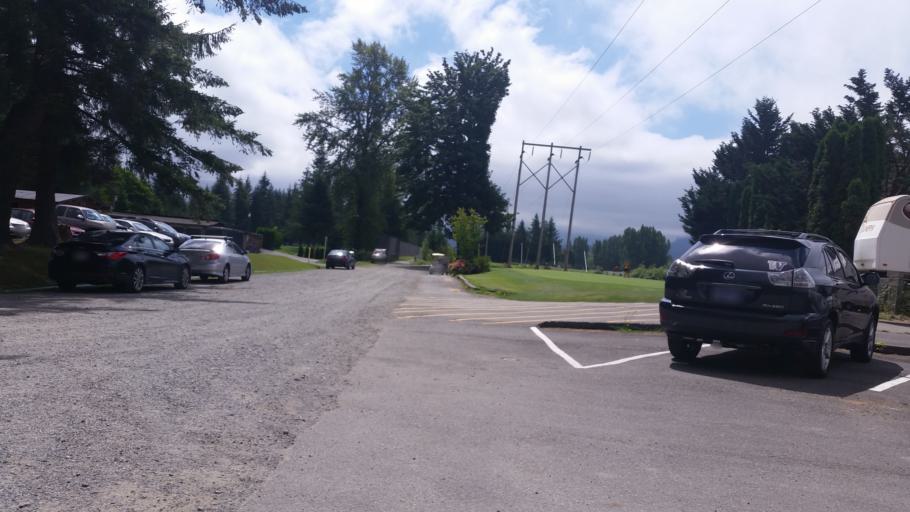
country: US
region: Washington
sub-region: King County
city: North Bend
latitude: 47.5193
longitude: -121.7993
